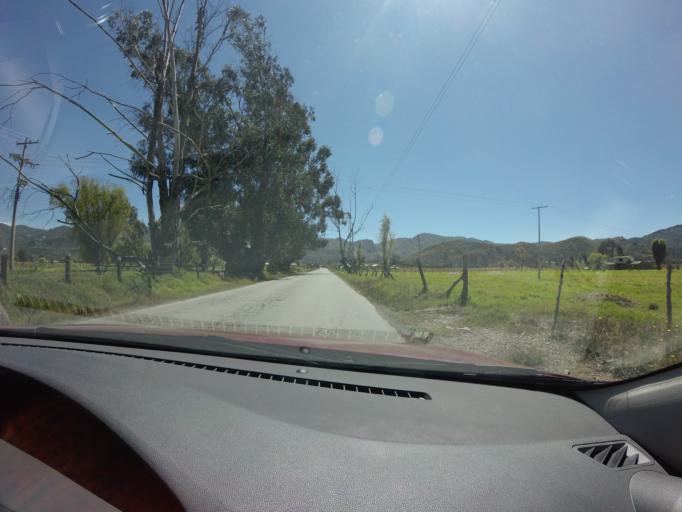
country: CO
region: Cundinamarca
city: Cucunuba
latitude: 5.2571
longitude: -73.7850
